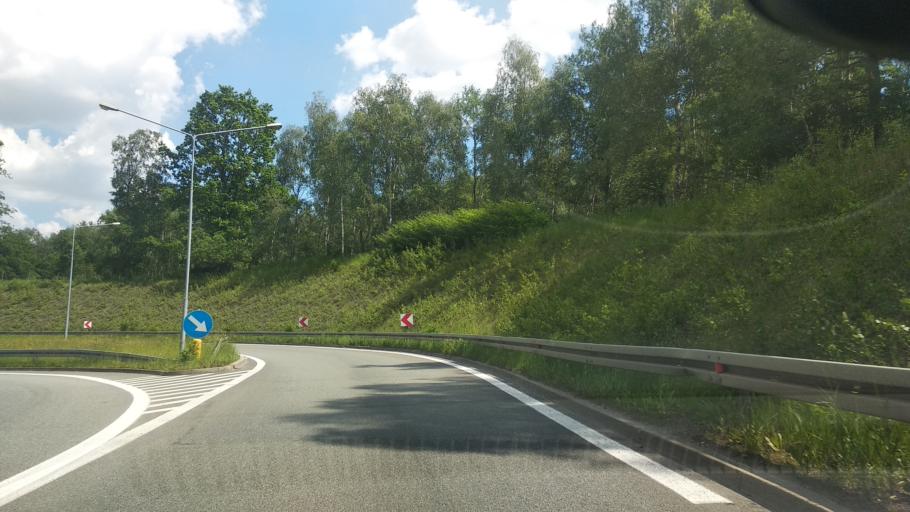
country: PL
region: Silesian Voivodeship
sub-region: Swietochlowice
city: Swietochlowice
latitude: 50.2539
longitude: 18.9469
